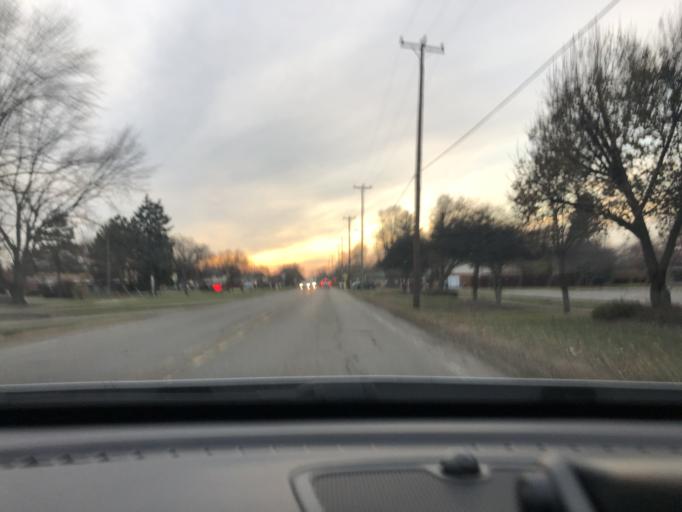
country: US
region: Michigan
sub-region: Wayne County
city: Taylor
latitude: 42.2418
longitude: -83.2476
